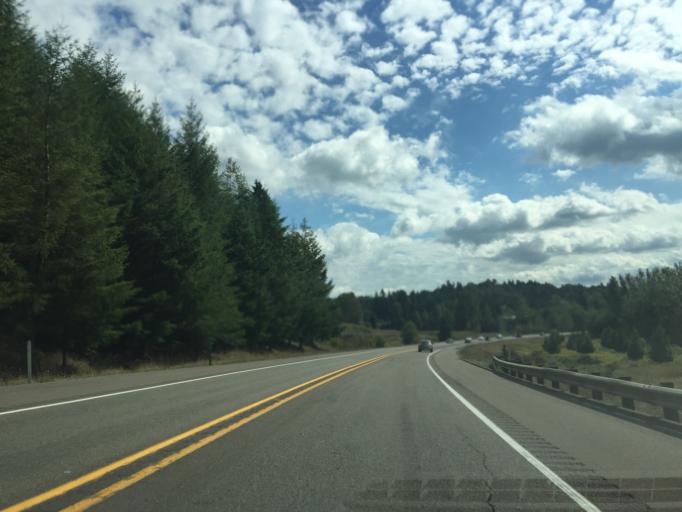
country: US
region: Washington
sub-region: Snohomish County
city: Snohomish
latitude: 47.9420
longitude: -122.0719
